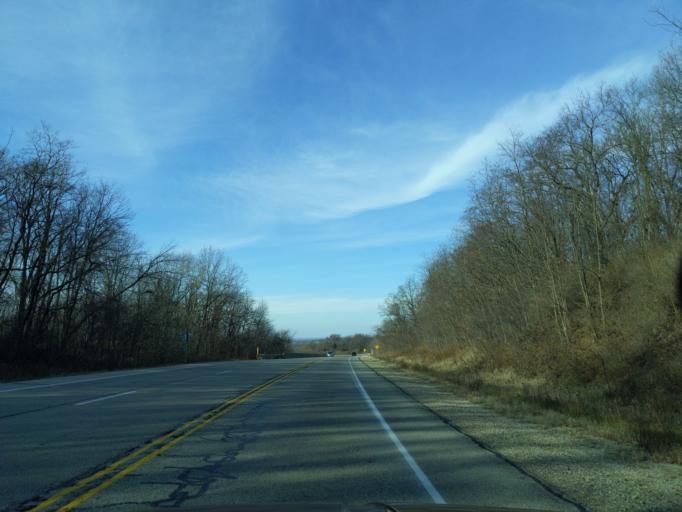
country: US
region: Wisconsin
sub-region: Walworth County
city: Whitewater
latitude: 42.8011
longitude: -88.6485
